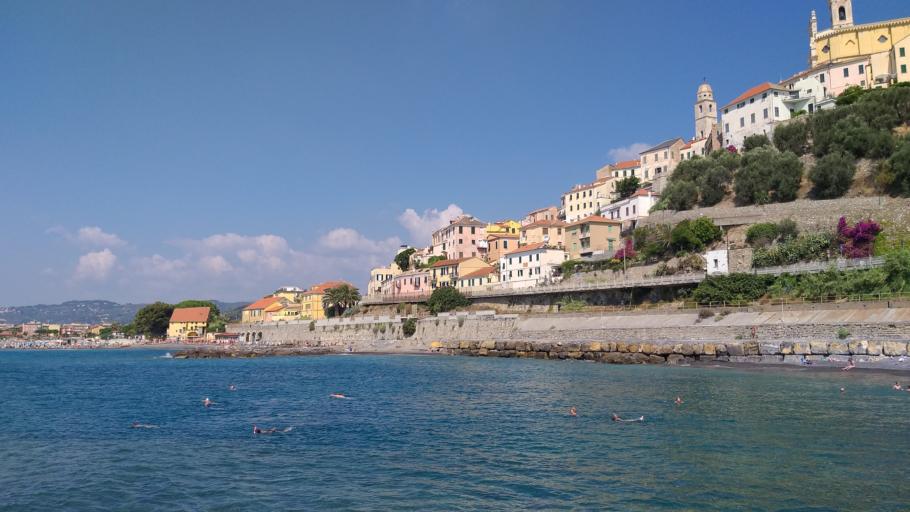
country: IT
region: Liguria
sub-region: Provincia di Imperia
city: Cervo
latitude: 43.9247
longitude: 8.1175
